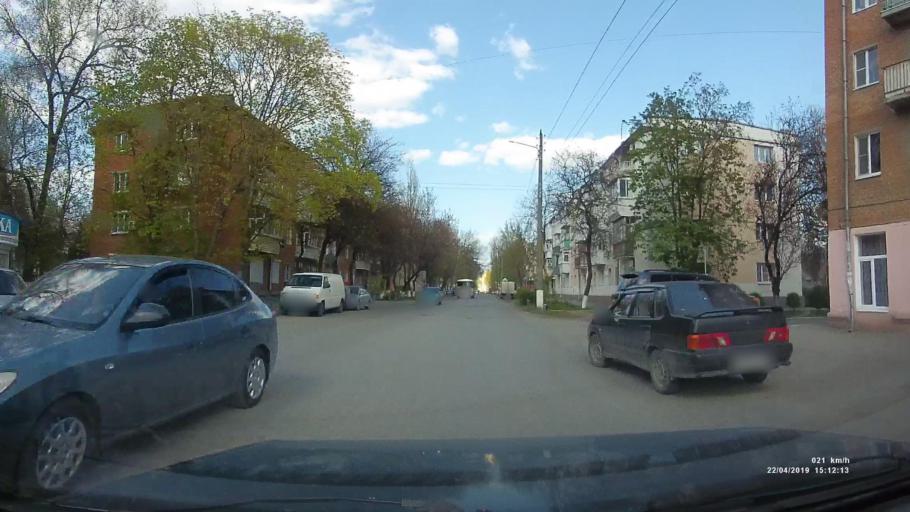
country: RU
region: Rostov
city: Azov
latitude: 47.0996
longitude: 39.4188
